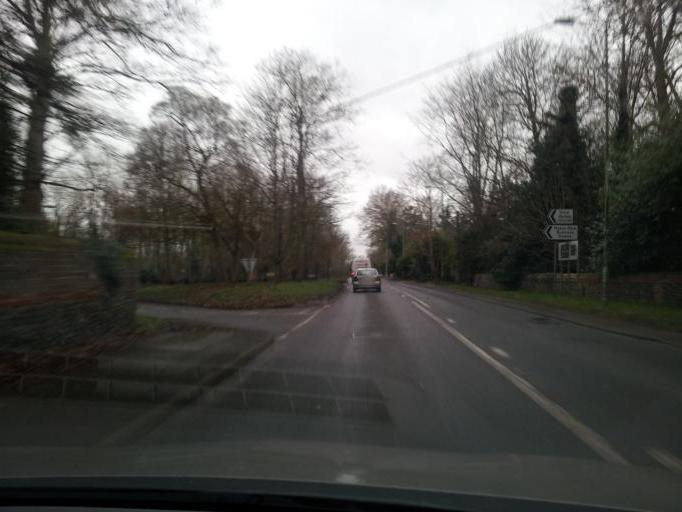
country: GB
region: England
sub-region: Suffolk
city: Great Barton
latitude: 52.2673
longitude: 0.7685
